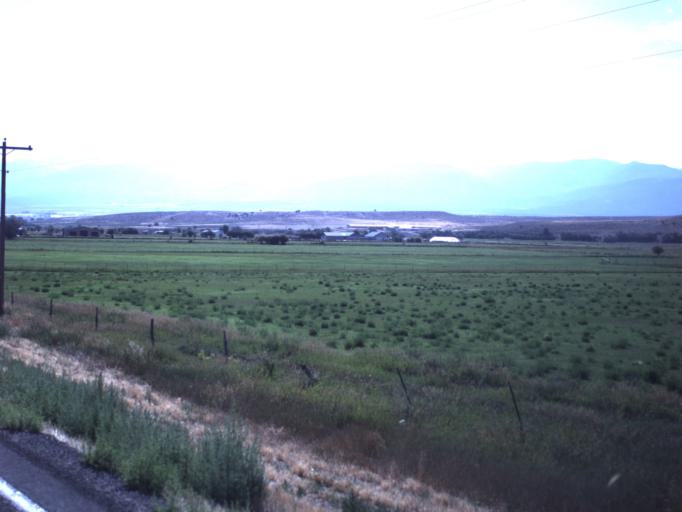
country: US
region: Utah
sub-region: Sanpete County
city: Moroni
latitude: 39.5258
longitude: -111.5552
